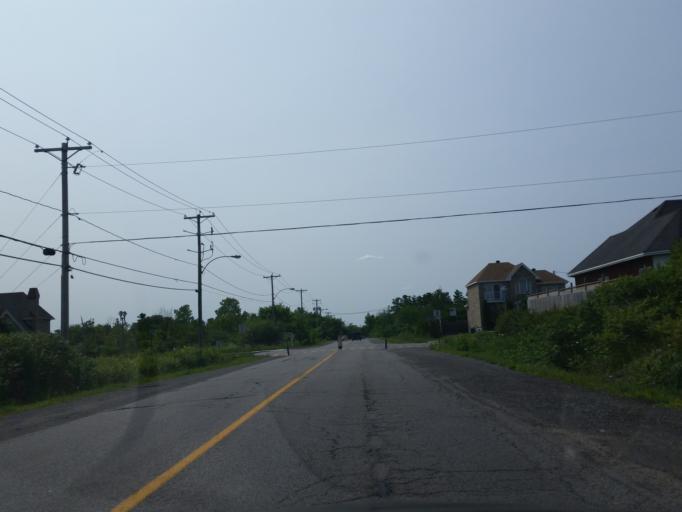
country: CA
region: Ontario
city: Bells Corners
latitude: 45.3861
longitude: -75.8293
